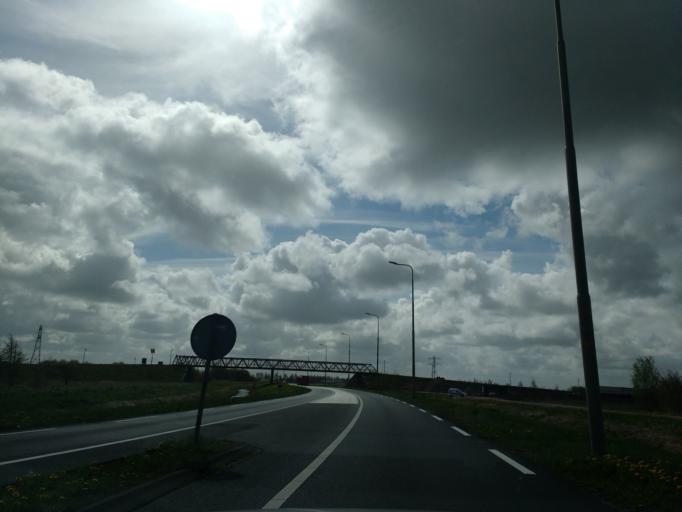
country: NL
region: North Holland
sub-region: Gemeente Bloemendaal
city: Bennebroek
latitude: 52.3008
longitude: 4.6187
